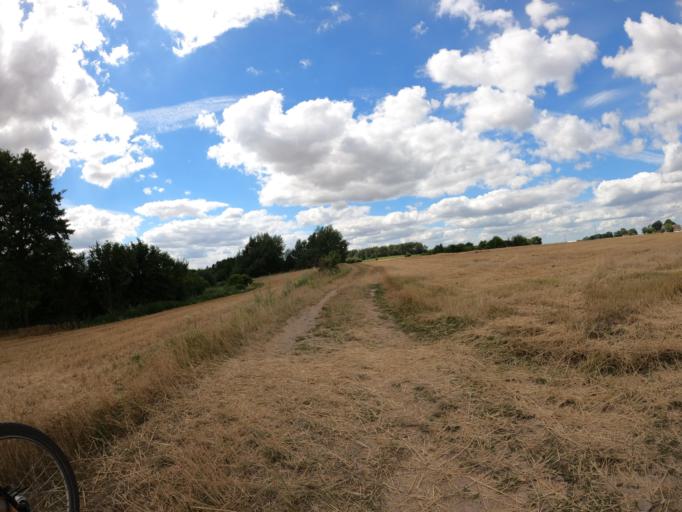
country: PL
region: West Pomeranian Voivodeship
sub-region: Powiat swidwinski
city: Swidwin
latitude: 53.7543
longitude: 15.8360
